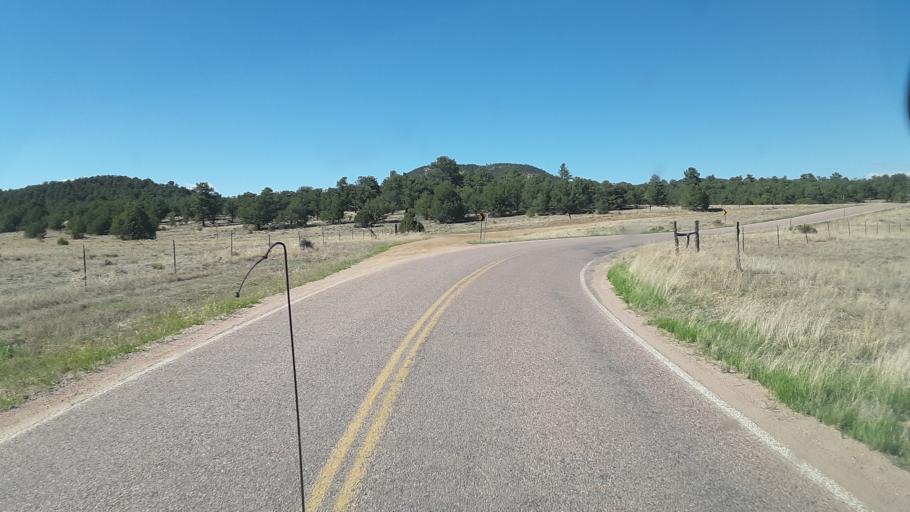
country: US
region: Colorado
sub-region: Custer County
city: Westcliffe
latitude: 38.3542
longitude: -105.4811
